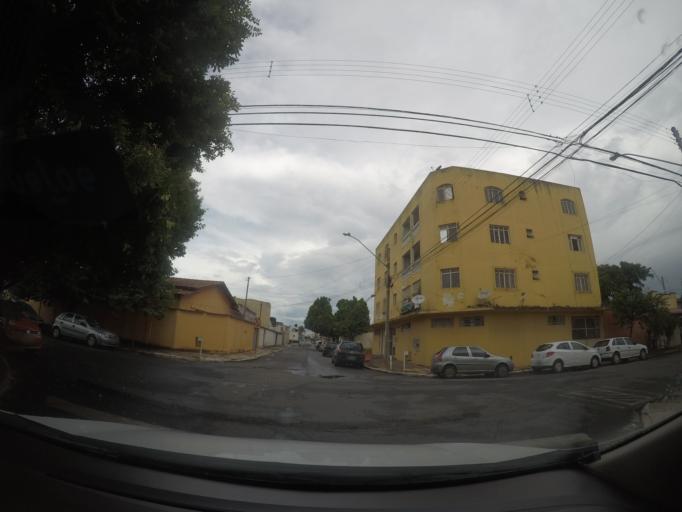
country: BR
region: Goias
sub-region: Goiania
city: Goiania
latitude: -16.6684
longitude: -49.2875
